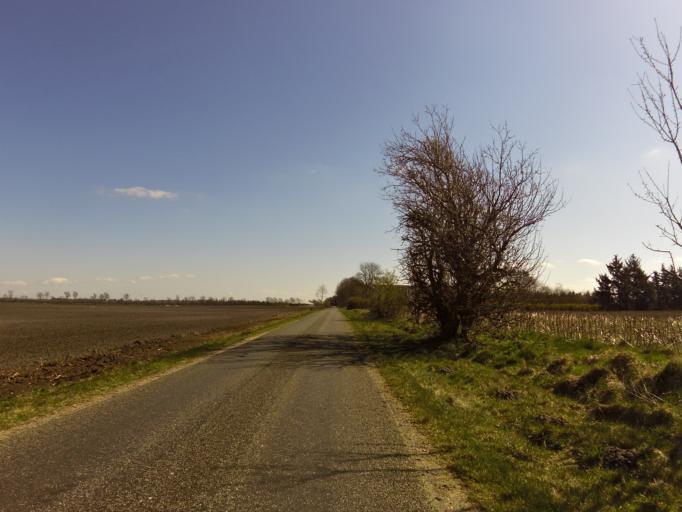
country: DK
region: South Denmark
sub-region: Esbjerg Kommune
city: Ribe
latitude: 55.3420
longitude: 8.8586
